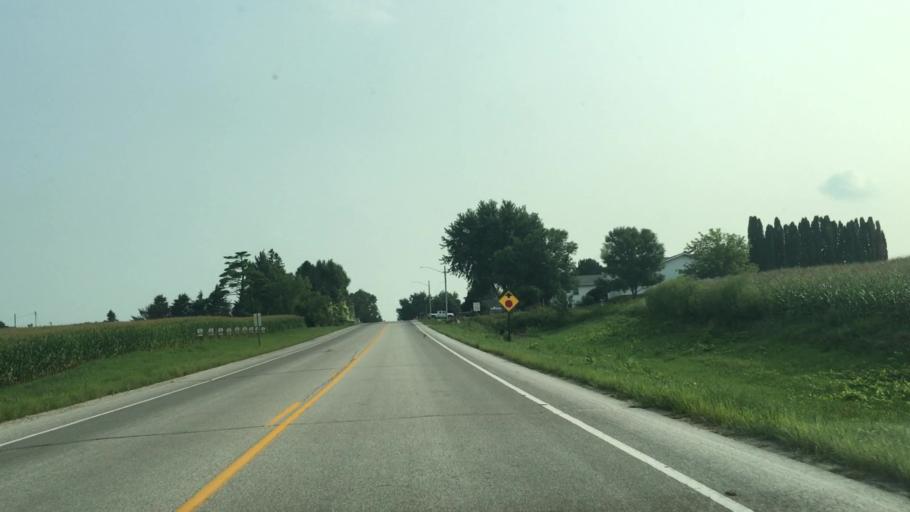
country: US
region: Minnesota
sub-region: Fillmore County
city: Harmony
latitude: 43.5357
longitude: -91.9297
